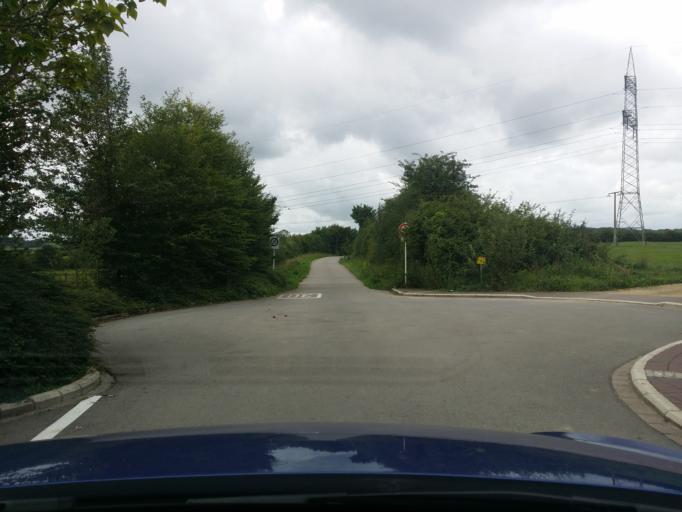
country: LU
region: Luxembourg
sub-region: Canton de Luxembourg
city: Bertrange
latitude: 49.6101
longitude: 6.0378
